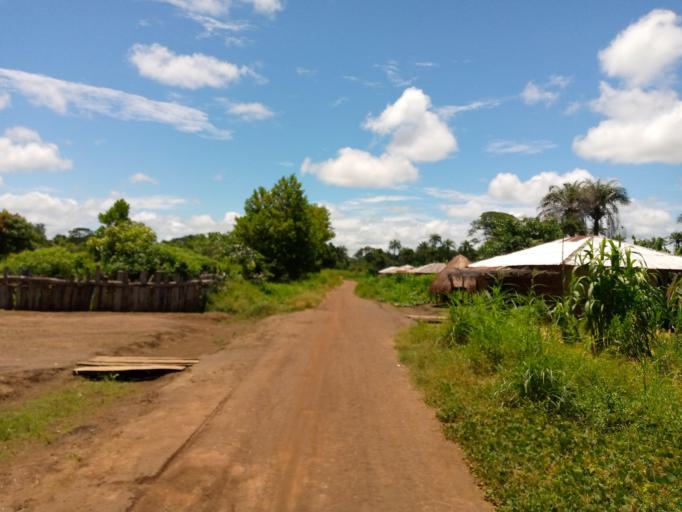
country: SL
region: Northern Province
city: Binkolo
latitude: 9.0609
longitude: -12.1509
